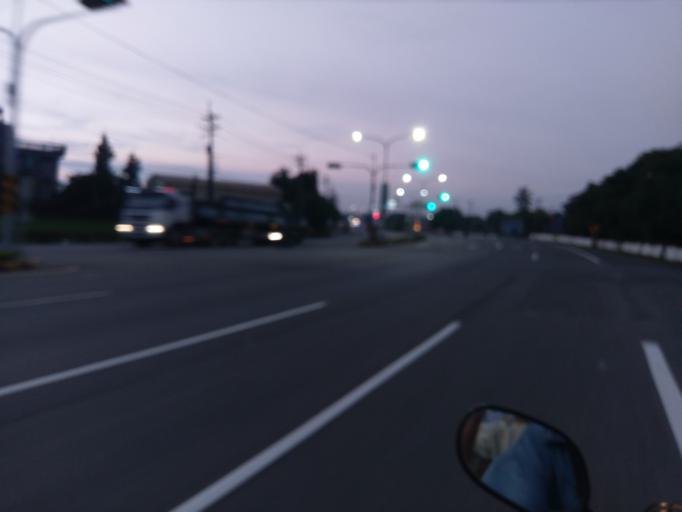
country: TW
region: Taiwan
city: Xinying
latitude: 23.1943
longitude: 120.3236
